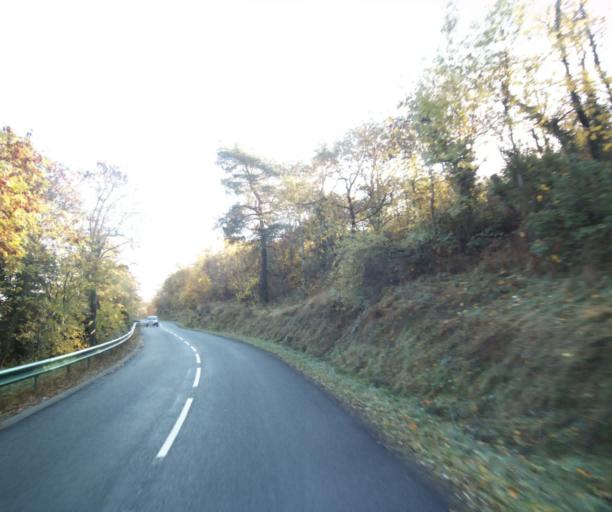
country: FR
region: Auvergne
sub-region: Departement du Puy-de-Dome
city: Nohanent
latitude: 45.8115
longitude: 3.0400
